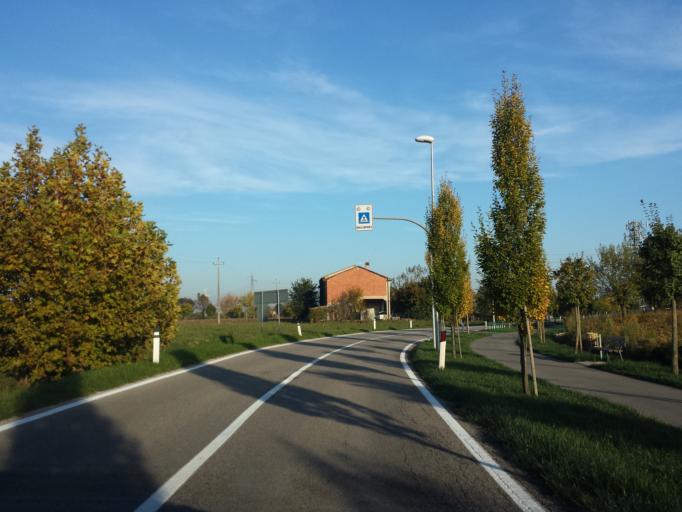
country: IT
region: Veneto
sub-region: Provincia di Vicenza
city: Motta
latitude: 45.5950
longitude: 11.5020
